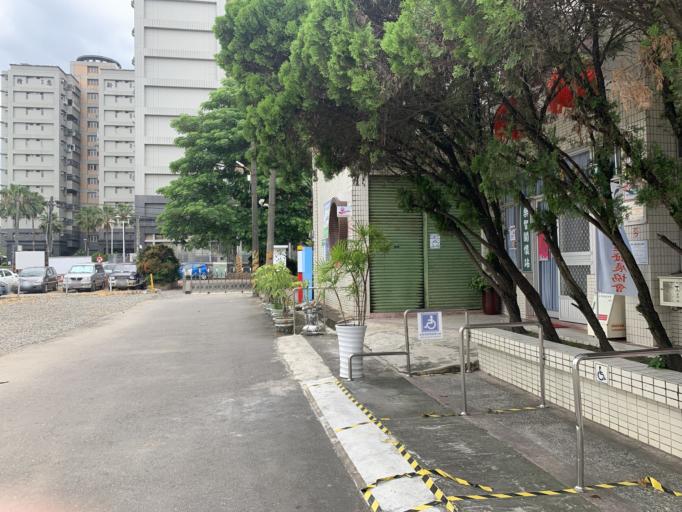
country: TW
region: Taiwan
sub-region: Chiayi
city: Jiayi Shi
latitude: 23.4916
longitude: 120.4767
